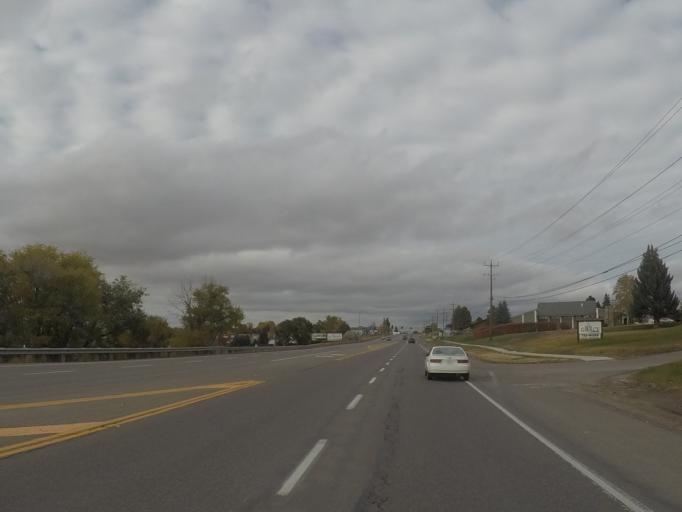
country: US
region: Montana
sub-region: Flathead County
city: Kalispell
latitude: 48.2112
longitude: -114.3270
